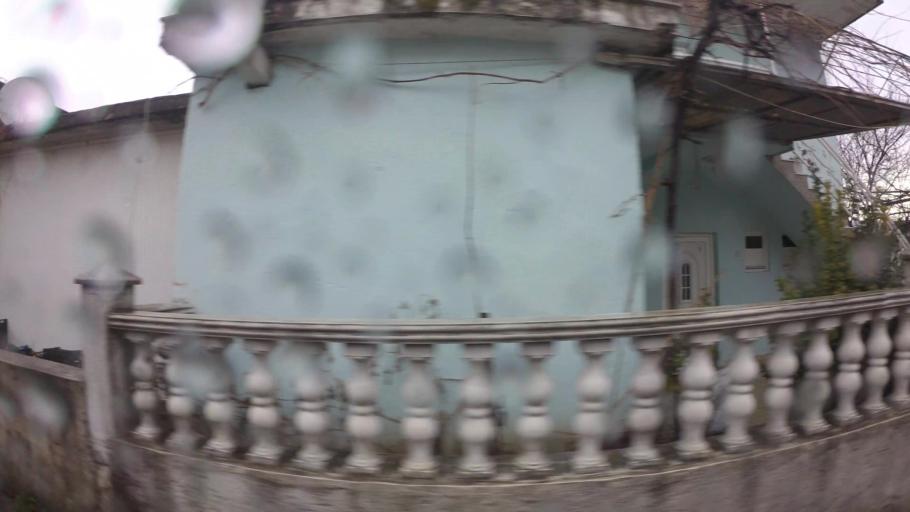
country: BA
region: Federation of Bosnia and Herzegovina
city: Cim
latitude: 43.3501
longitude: 17.7836
